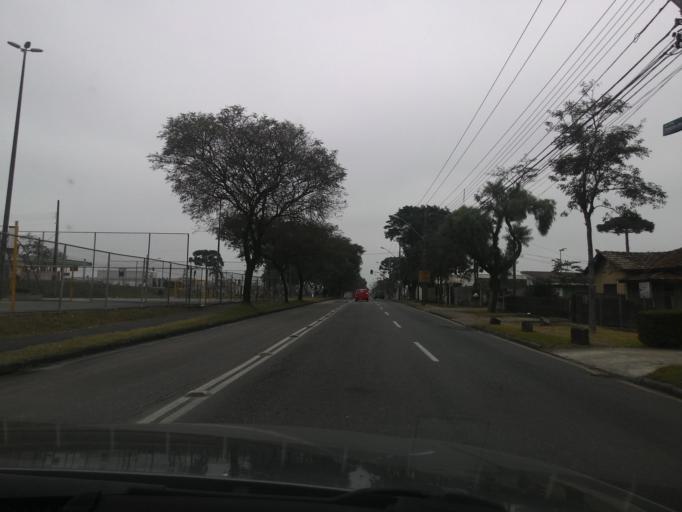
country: BR
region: Parana
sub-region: Curitiba
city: Curitiba
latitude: -25.4750
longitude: -49.2753
